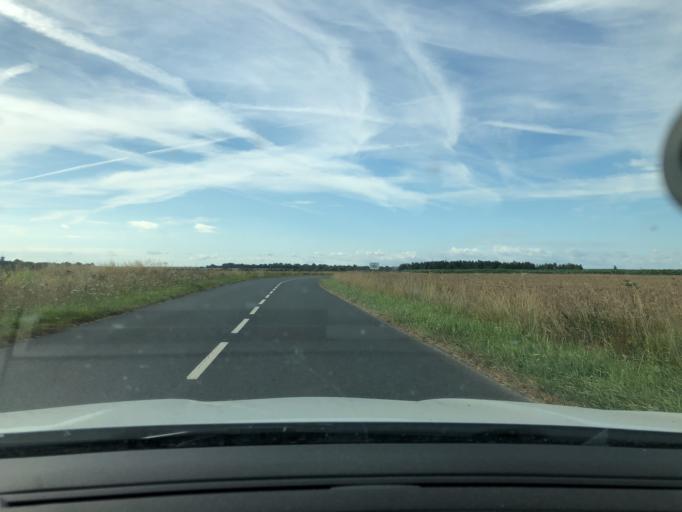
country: FR
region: Lower Normandy
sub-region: Departement du Calvados
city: Saint-Vigor-le-Grand
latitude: 49.2522
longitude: -0.6229
